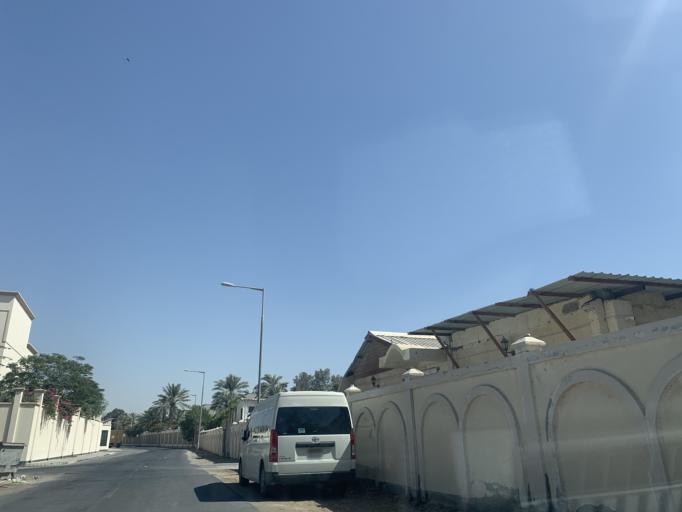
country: BH
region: Manama
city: Jidd Hafs
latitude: 26.2252
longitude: 50.4993
